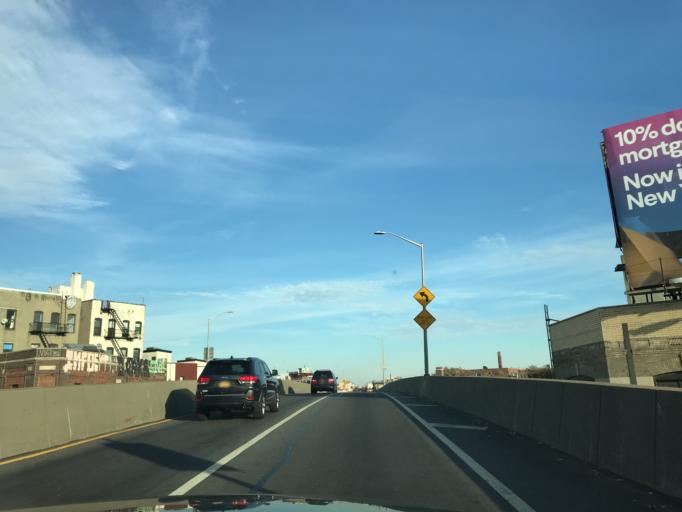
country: US
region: New York
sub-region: Queens County
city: Long Island City
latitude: 40.7102
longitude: -73.9586
